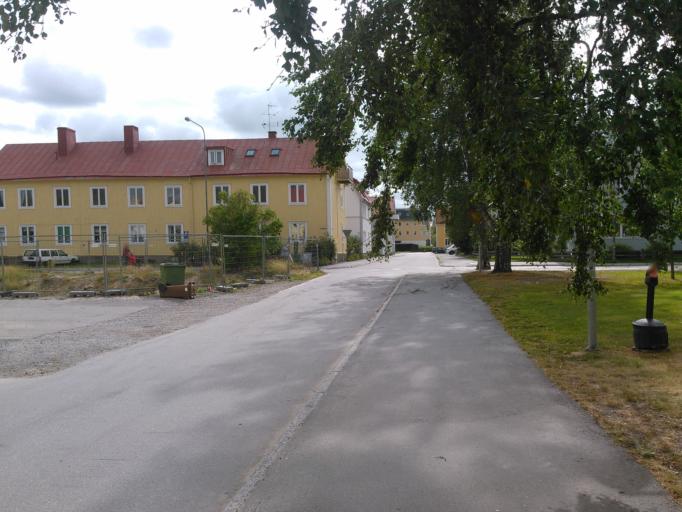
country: SE
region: Vaesterbotten
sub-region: Umea Kommun
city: Umea
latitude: 63.8309
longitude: 20.2474
